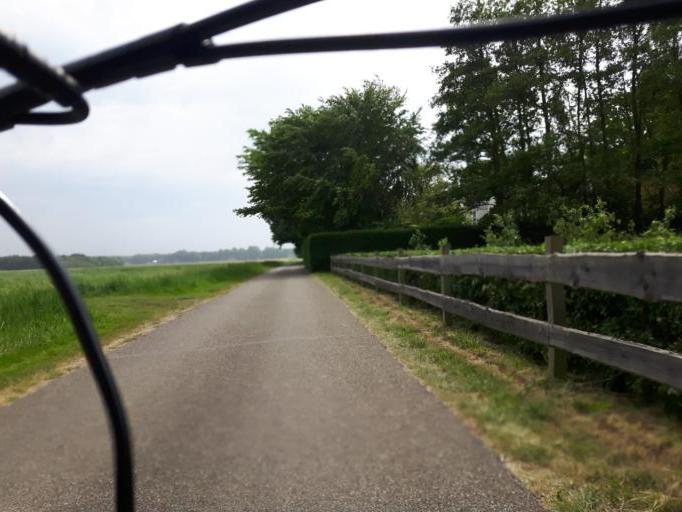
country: NL
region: North Brabant
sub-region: Gemeente Bergen op Zoom
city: Lepelstraat
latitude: 51.5389
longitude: 4.3136
